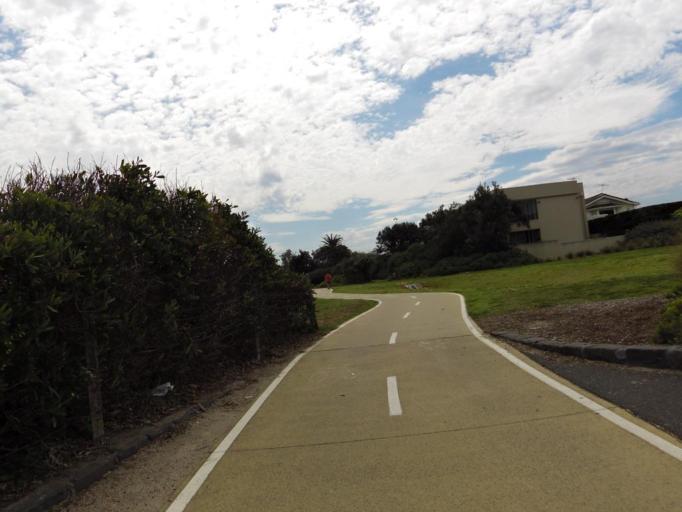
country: AU
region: Victoria
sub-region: Port Phillip
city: Elwood
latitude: -37.8931
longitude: 144.9861
